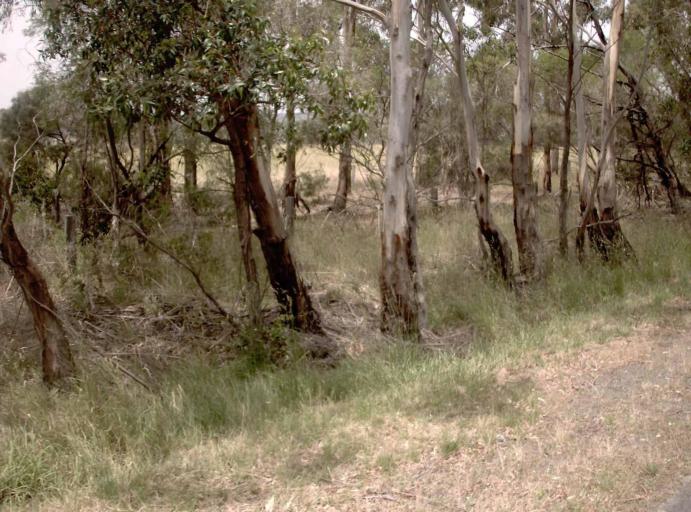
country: AU
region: Victoria
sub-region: Latrobe
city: Traralgon
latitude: -38.4884
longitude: 146.7138
